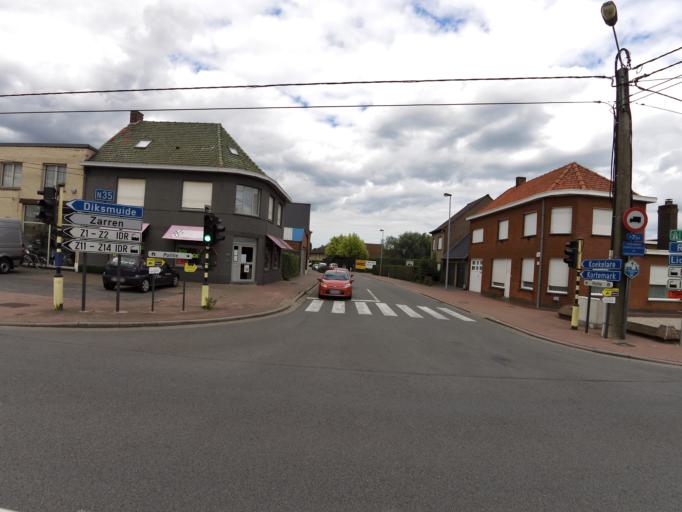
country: BE
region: Flanders
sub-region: Provincie West-Vlaanderen
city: Kortemark
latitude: 51.0226
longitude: 3.0448
